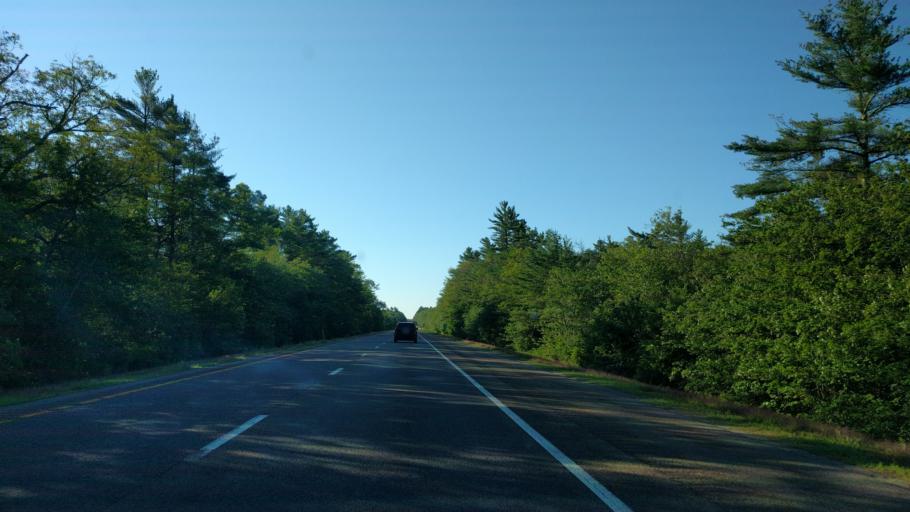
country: US
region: Massachusetts
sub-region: Plymouth County
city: West Wareham
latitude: 41.8348
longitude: -70.8215
